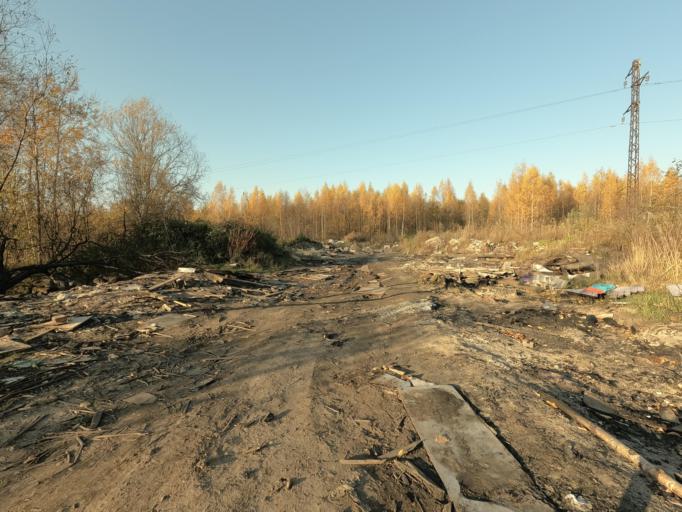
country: RU
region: Leningrad
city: Kirovsk
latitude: 59.8625
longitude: 31.0121
